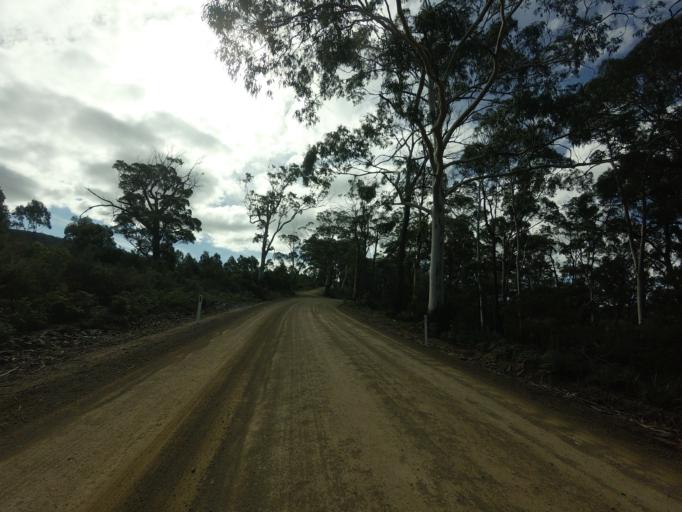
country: AU
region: Tasmania
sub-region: Clarence
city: Sandford
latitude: -43.0950
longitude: 147.7220
